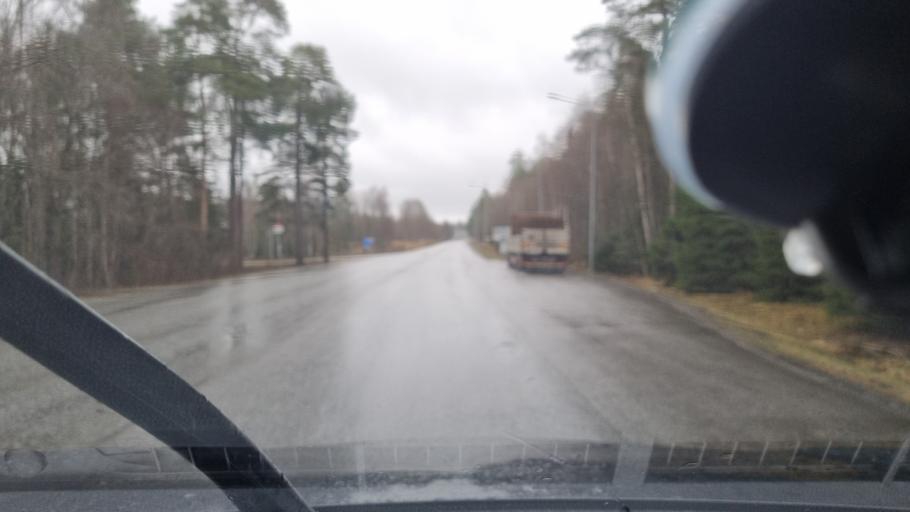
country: SE
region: Stockholm
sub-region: Upplands-Bro Kommun
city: Kungsaengen
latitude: 59.5140
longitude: 17.7581
